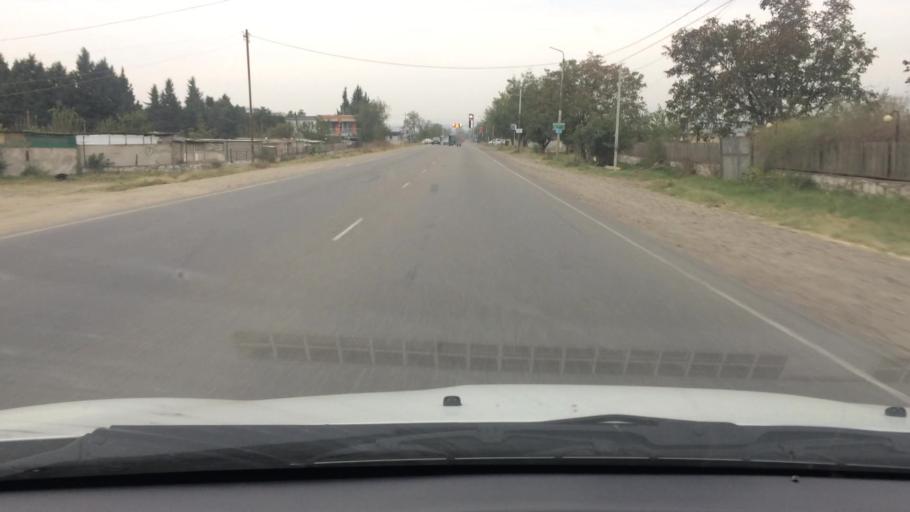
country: GE
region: Kvemo Kartli
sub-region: Marneuli
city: Marneuli
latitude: 41.5768
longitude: 44.7747
